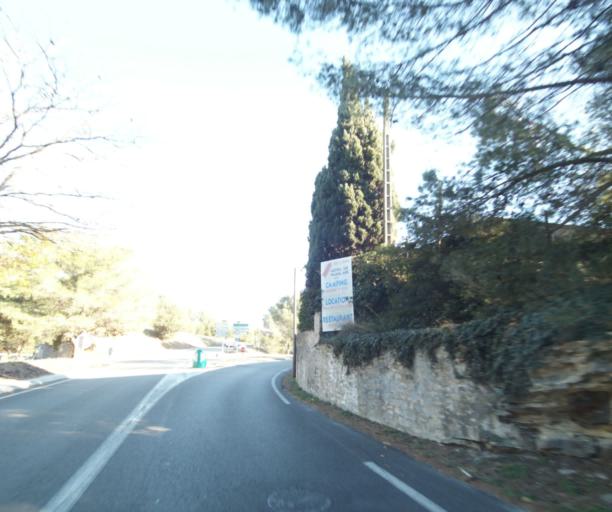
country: FR
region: Provence-Alpes-Cote d'Azur
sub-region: Departement des Bouches-du-Rhone
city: La Ciotat
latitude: 43.1945
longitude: 5.5994
